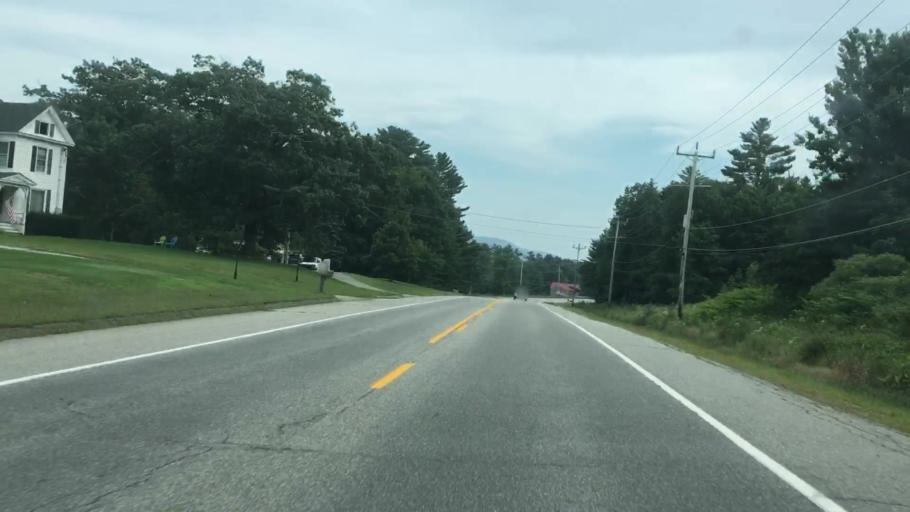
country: US
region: Maine
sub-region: Oxford County
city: Bethel
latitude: 44.4341
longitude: -70.8036
